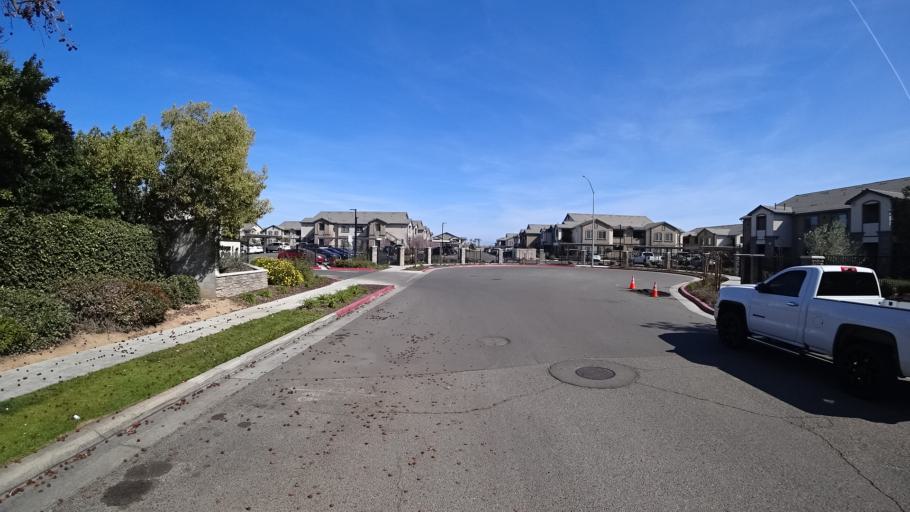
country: US
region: California
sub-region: Fresno County
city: Clovis
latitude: 36.8395
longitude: -119.7344
